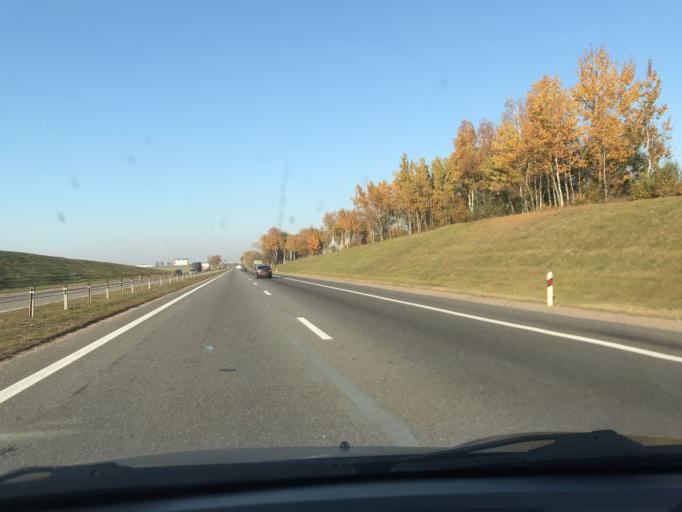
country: BY
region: Minsk
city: Samakhvalavichy
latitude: 53.7737
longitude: 27.5235
